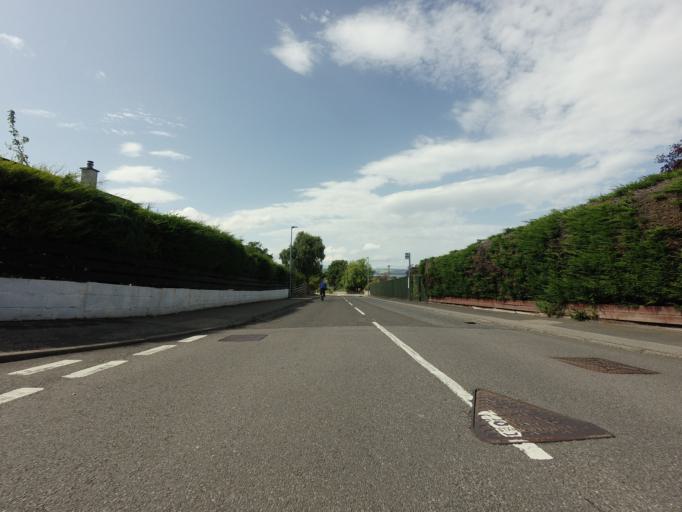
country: GB
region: Scotland
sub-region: Highland
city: Fortrose
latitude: 57.4946
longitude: -4.1141
